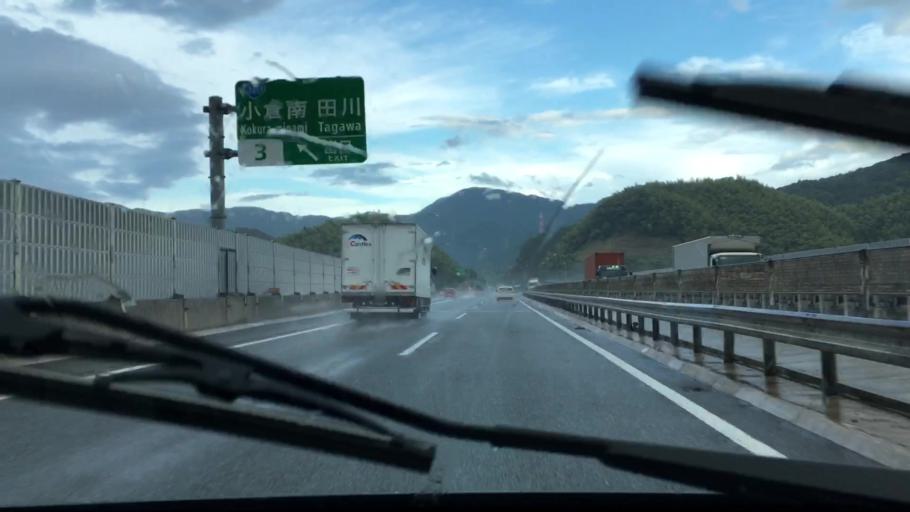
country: JP
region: Fukuoka
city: Kitakyushu
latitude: 33.8054
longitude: 130.8496
